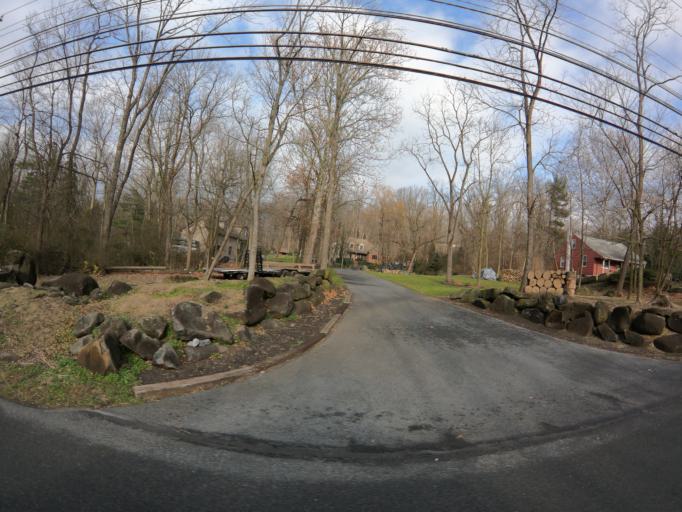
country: US
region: Pennsylvania
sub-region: Lancaster County
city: Elizabethtown
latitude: 40.1598
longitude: -76.6306
